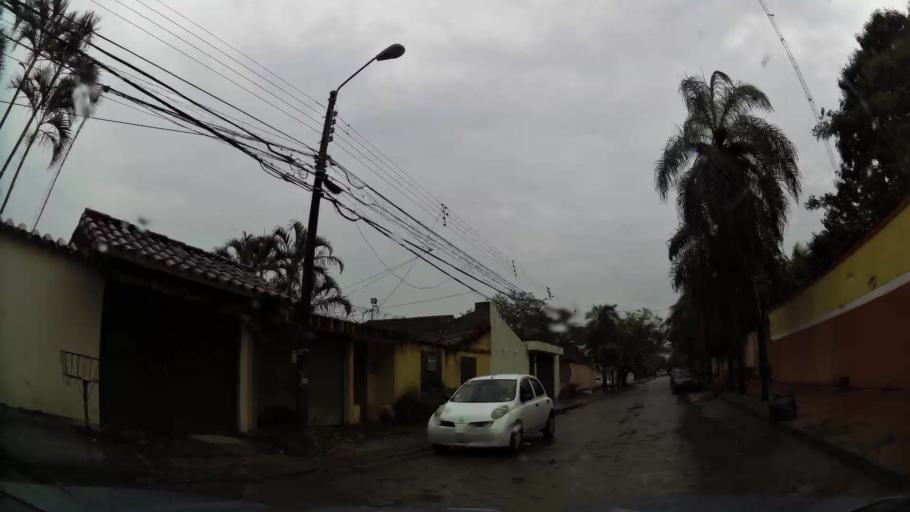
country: BO
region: Santa Cruz
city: Santa Cruz de la Sierra
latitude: -17.7876
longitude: -63.2086
